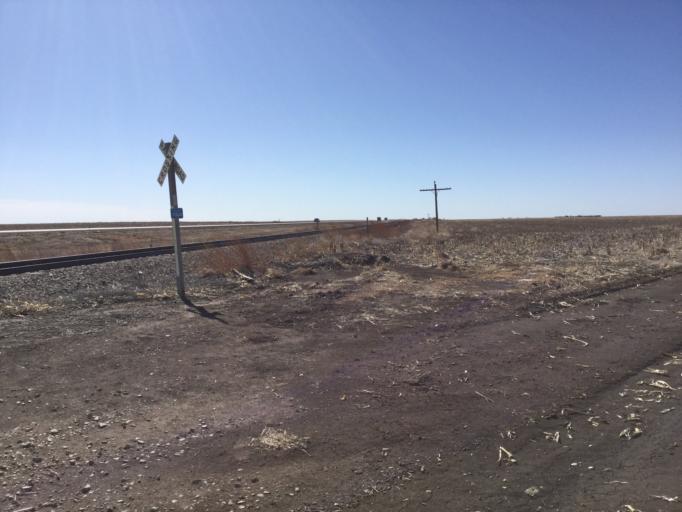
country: US
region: Kansas
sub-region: Sheridan County
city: Hoxie
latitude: 39.5243
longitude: -100.6149
